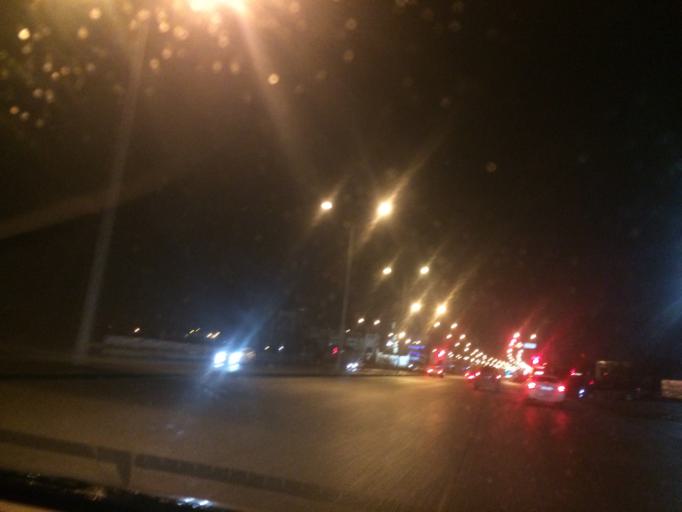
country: KZ
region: Astana Qalasy
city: Astana
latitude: 51.1758
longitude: 71.3982
